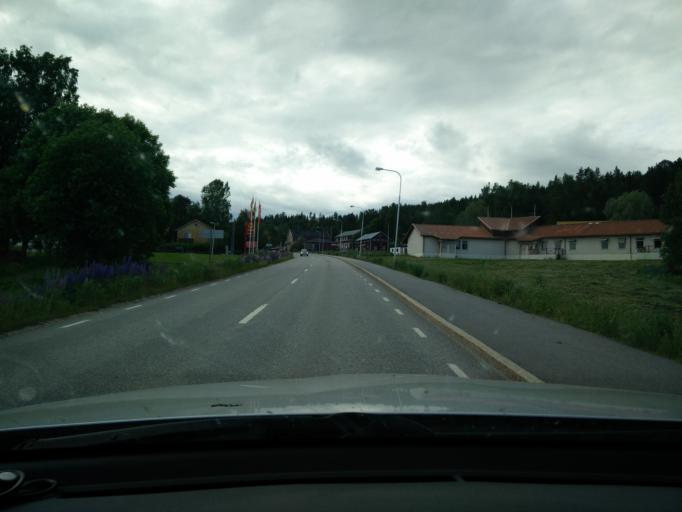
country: SE
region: Gaevleborg
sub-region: Hudiksvalls Kommun
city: Delsbo
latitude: 62.1085
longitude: 16.7141
